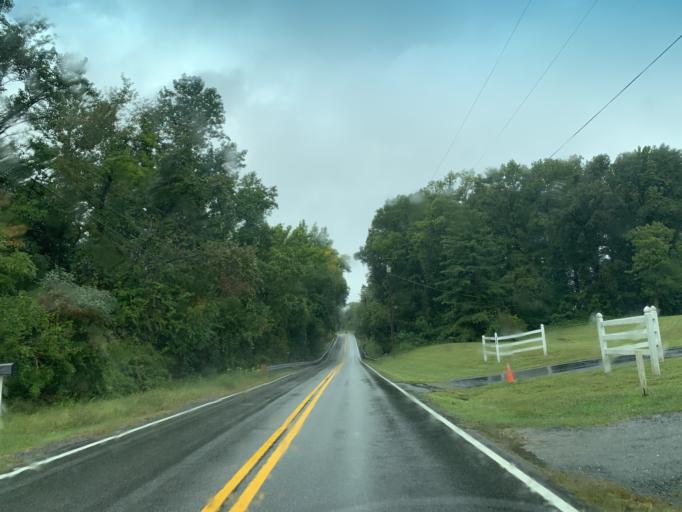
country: US
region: Maryland
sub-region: Queen Anne's County
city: Kingstown
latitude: 39.2615
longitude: -75.8534
